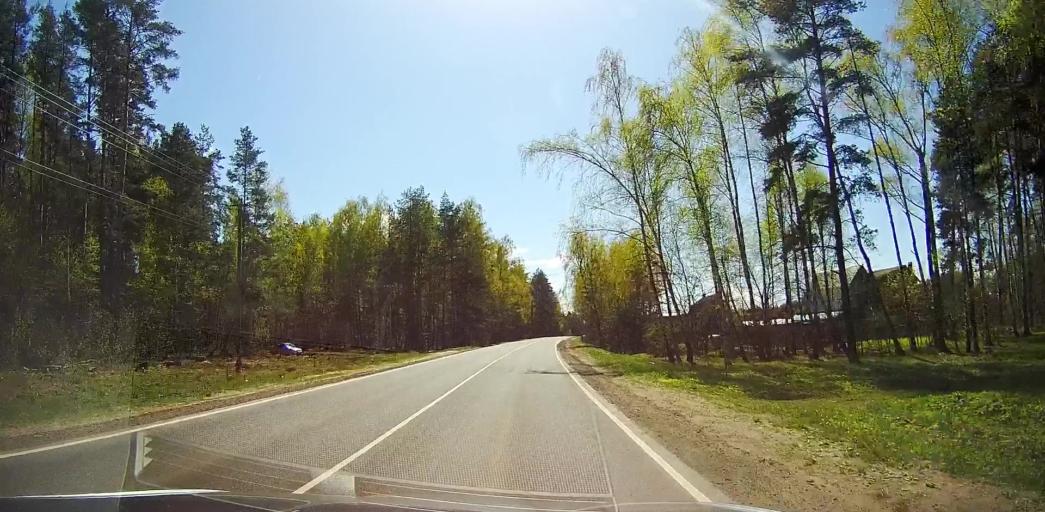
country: RU
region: Moskovskaya
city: Beloozerskiy
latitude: 55.4982
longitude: 38.4308
